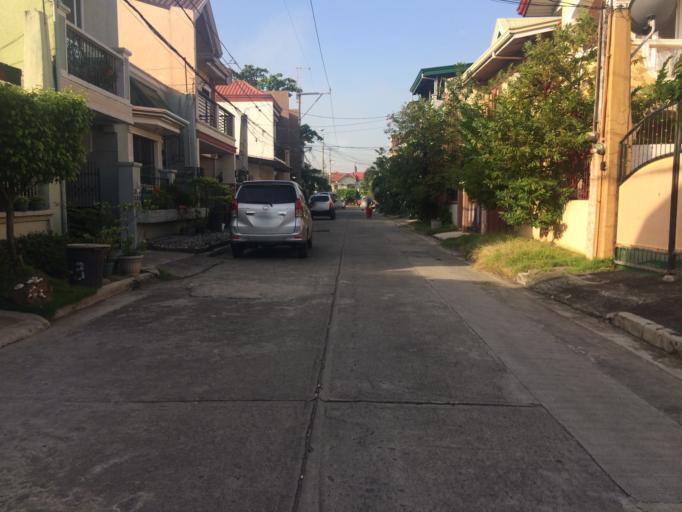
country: PH
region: Calabarzon
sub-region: Province of Rizal
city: Taytay
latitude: 14.5520
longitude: 121.1063
